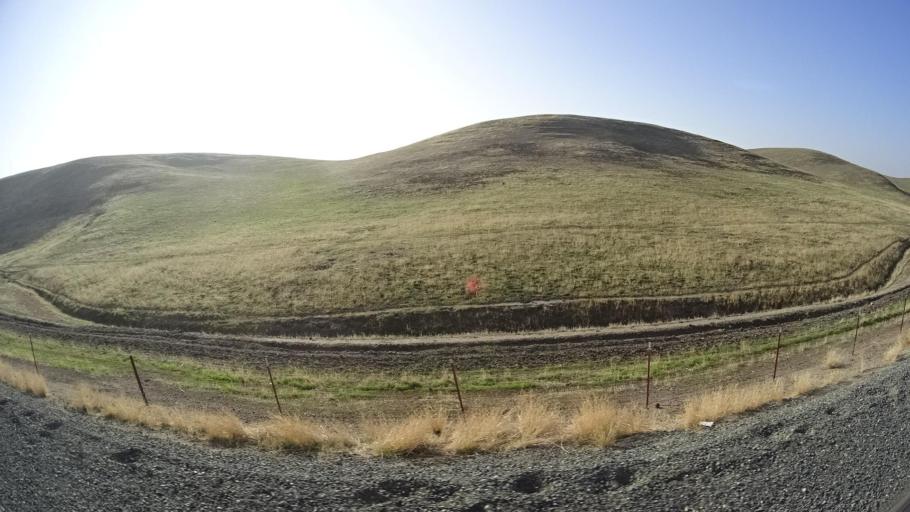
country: US
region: California
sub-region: Tulare County
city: Richgrove
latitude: 35.7448
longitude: -118.9363
